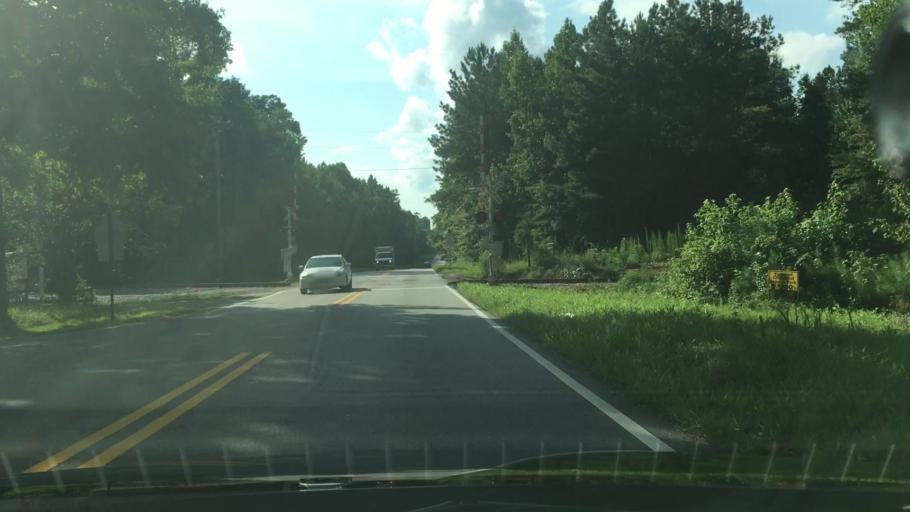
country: US
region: Georgia
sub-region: Coweta County
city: East Newnan
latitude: 33.3459
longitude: -84.6925
